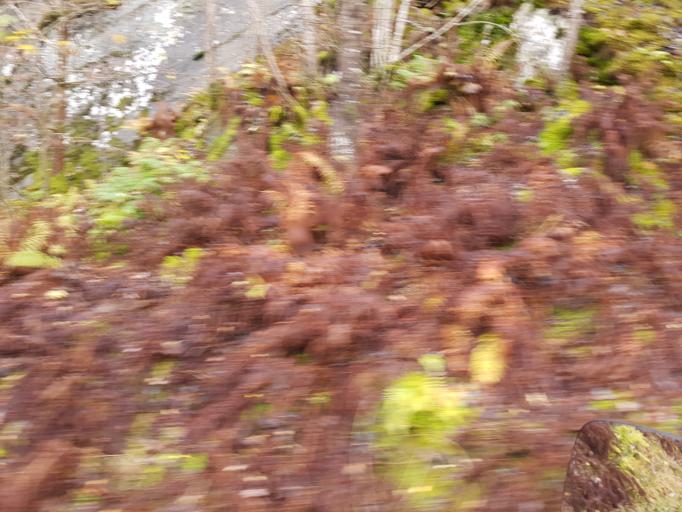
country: SE
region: Vaestra Goetaland
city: Svanesund
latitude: 58.1939
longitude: 11.8379
